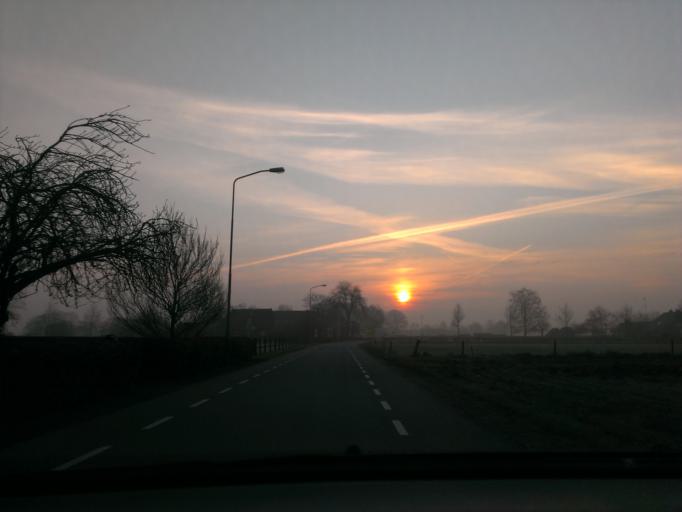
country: NL
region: Gelderland
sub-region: Gemeente Epe
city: Oene
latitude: 52.3473
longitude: 6.0355
